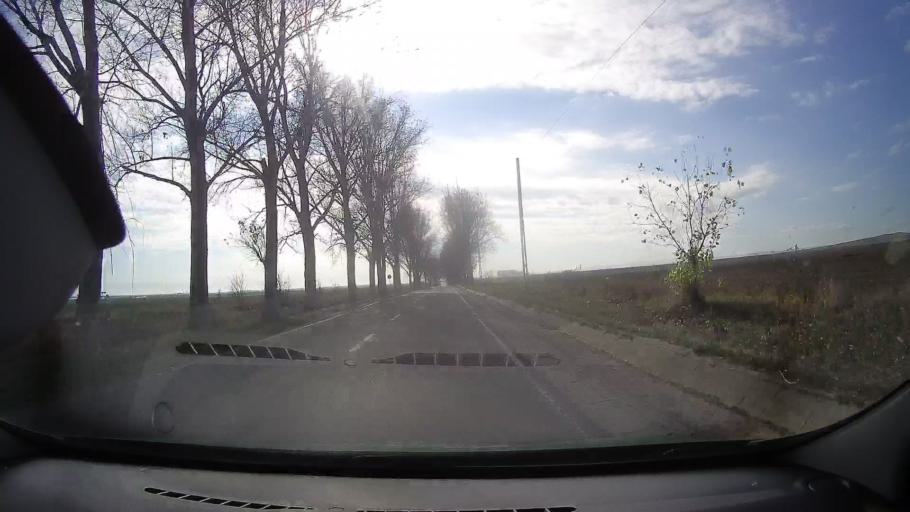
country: RO
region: Tulcea
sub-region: Comuna Valea Nucarilor
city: Agighiol
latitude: 45.0053
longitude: 28.8852
